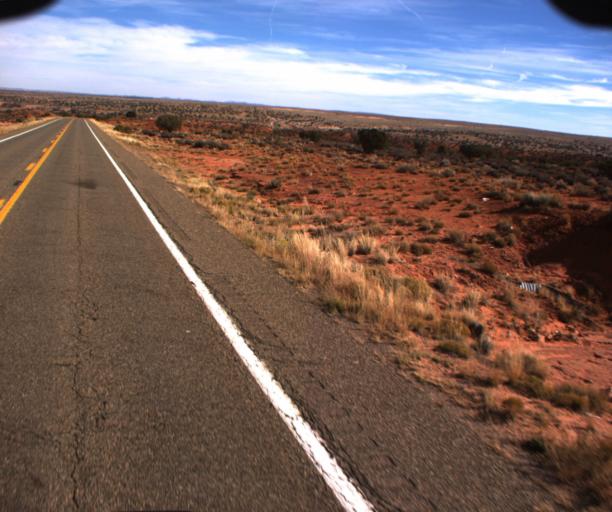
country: US
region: Arizona
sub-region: Coconino County
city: Kaibito
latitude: 36.6018
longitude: -111.0899
